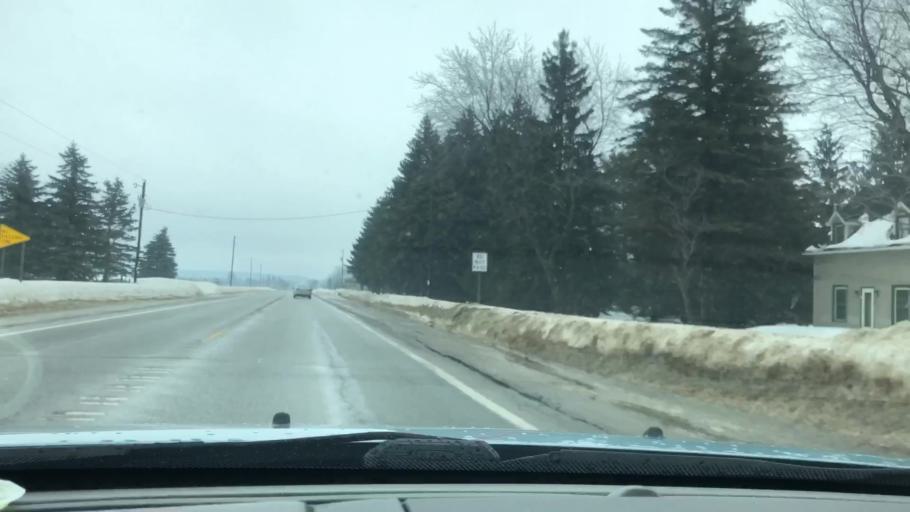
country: US
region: Michigan
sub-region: Charlevoix County
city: Boyne City
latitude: 45.0665
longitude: -84.8905
